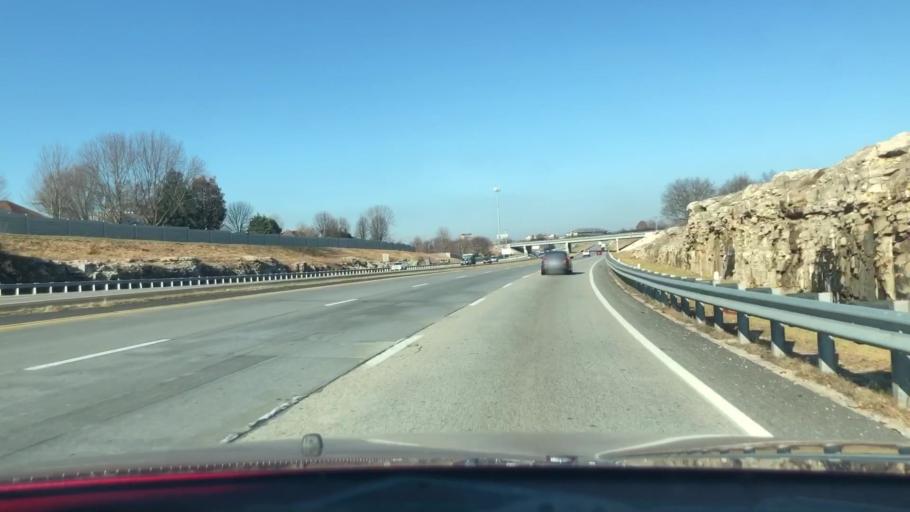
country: US
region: Missouri
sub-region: Greene County
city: Battlefield
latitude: 37.1358
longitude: -93.3065
